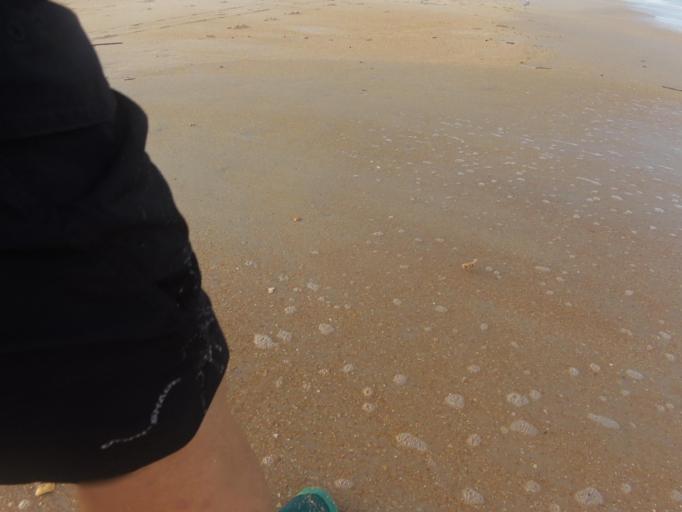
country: US
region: Florida
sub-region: Flagler County
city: Palm Coast
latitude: 29.6305
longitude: -81.1963
